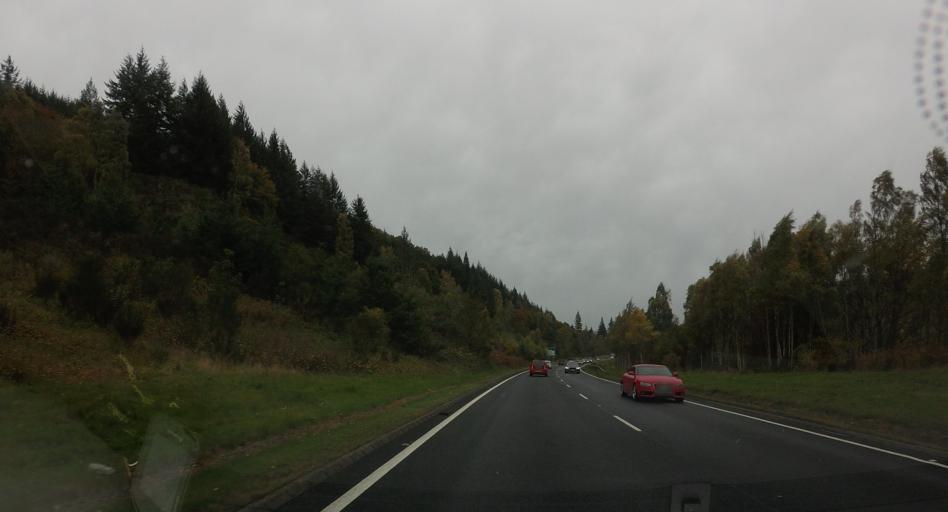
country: GB
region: Scotland
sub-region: Perth and Kinross
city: Bankfoot
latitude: 56.5830
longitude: -3.6209
